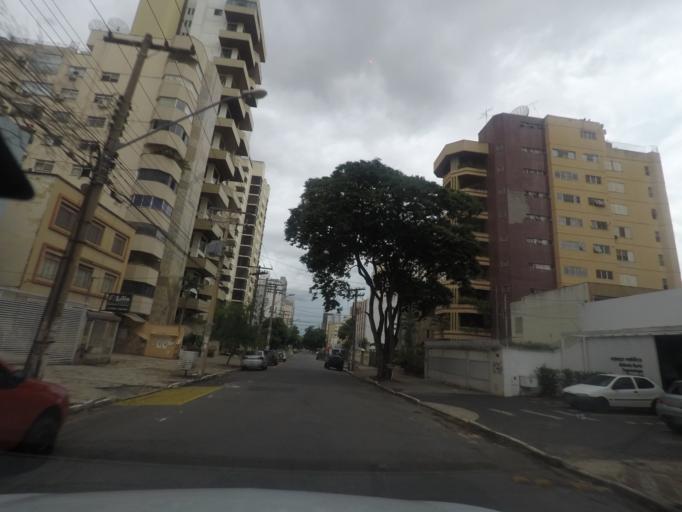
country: BR
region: Goias
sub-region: Goiania
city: Goiania
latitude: -16.6825
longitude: -49.2641
